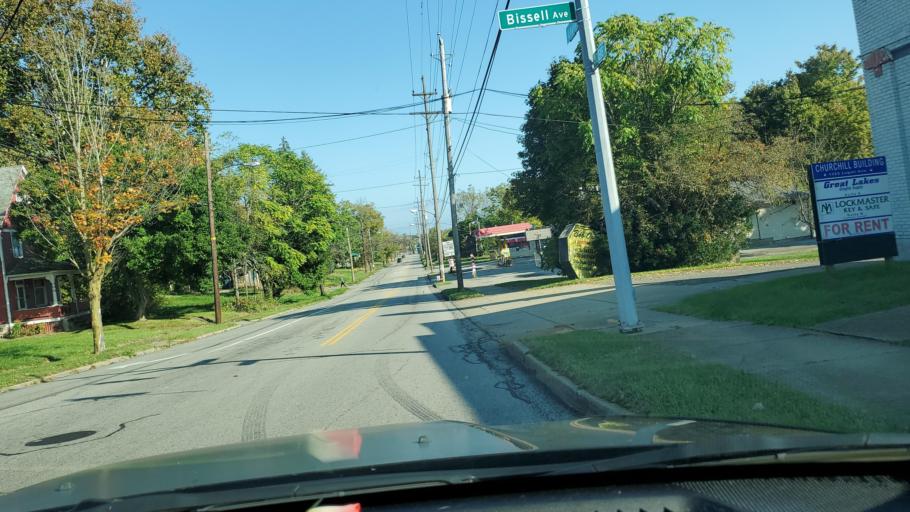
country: US
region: Ohio
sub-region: Mahoning County
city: Youngstown
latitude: 41.1177
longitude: -80.6384
